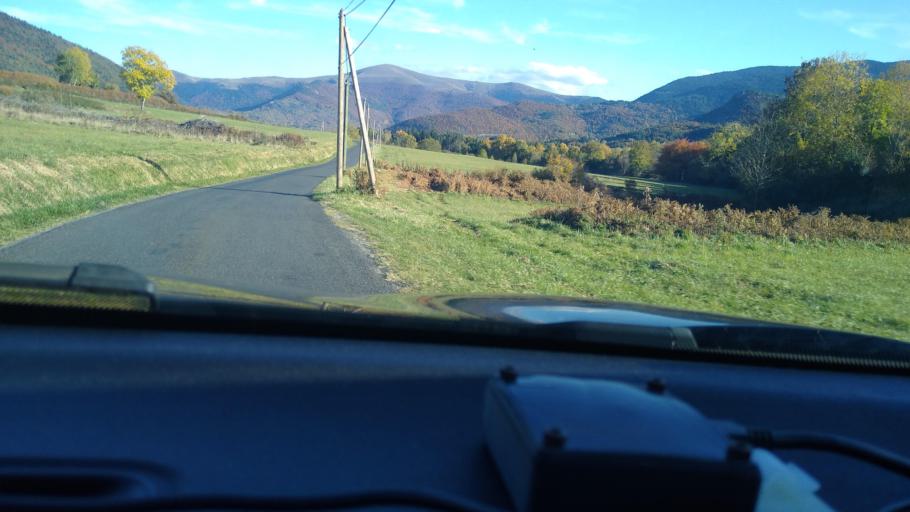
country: FR
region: Languedoc-Roussillon
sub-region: Departement de l'Aude
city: Quillan
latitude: 42.7468
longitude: 2.1752
